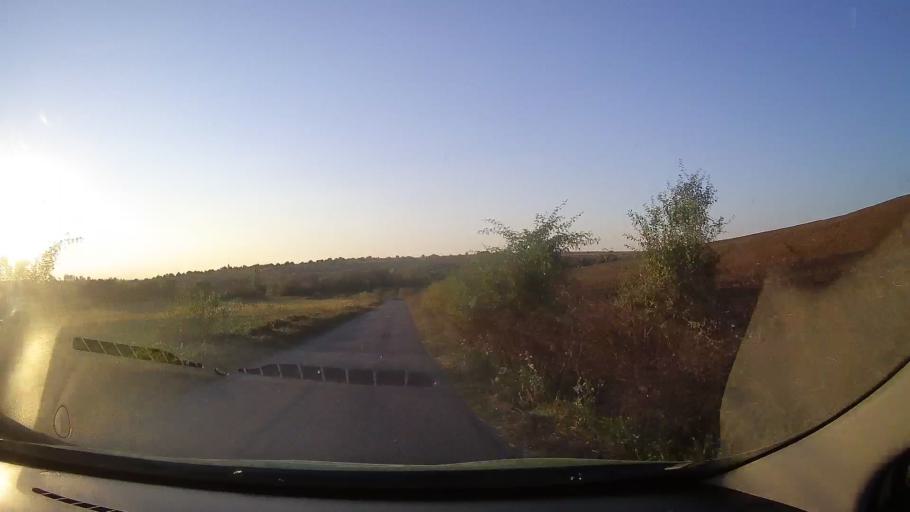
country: RO
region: Bihor
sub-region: Comuna Salard
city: Salard
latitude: 47.2492
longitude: 22.0155
